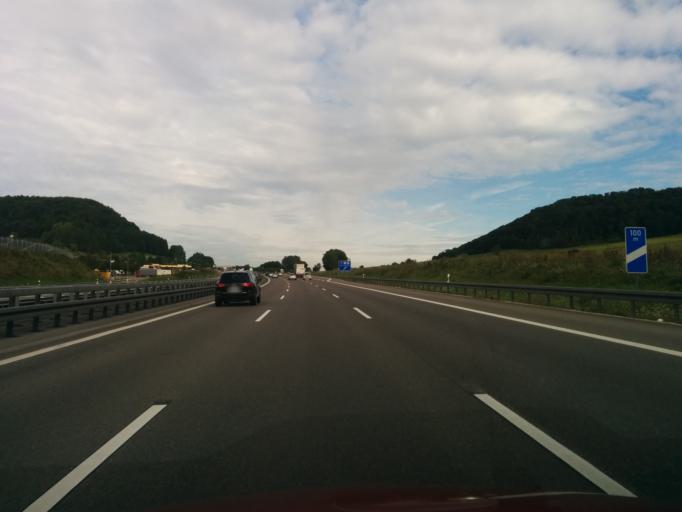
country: DE
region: Baden-Wuerttemberg
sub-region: Regierungsbezirk Stuttgart
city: Gruibingen
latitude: 48.6050
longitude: 9.6369
